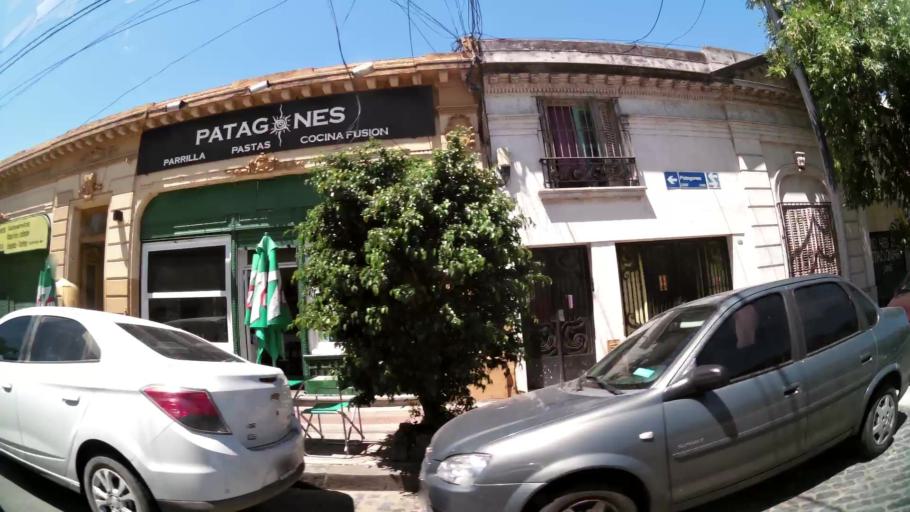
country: AR
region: Buenos Aires F.D.
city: Buenos Aires
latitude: -34.6382
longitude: -58.4049
